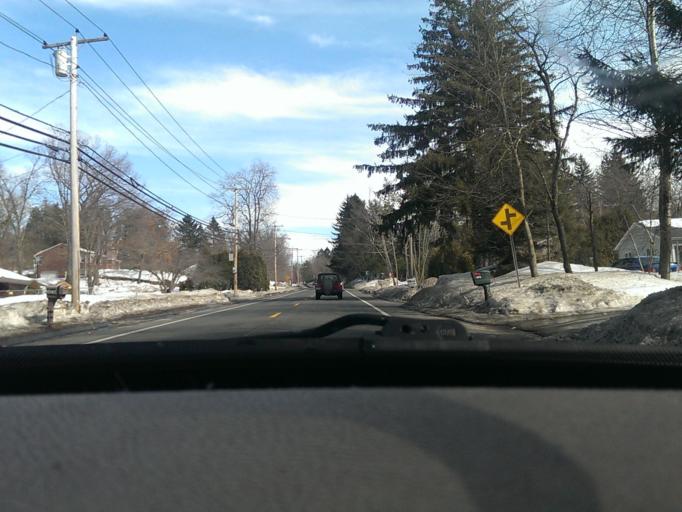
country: US
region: Massachusetts
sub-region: Hampden County
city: Wilbraham
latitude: 42.1527
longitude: -72.4065
